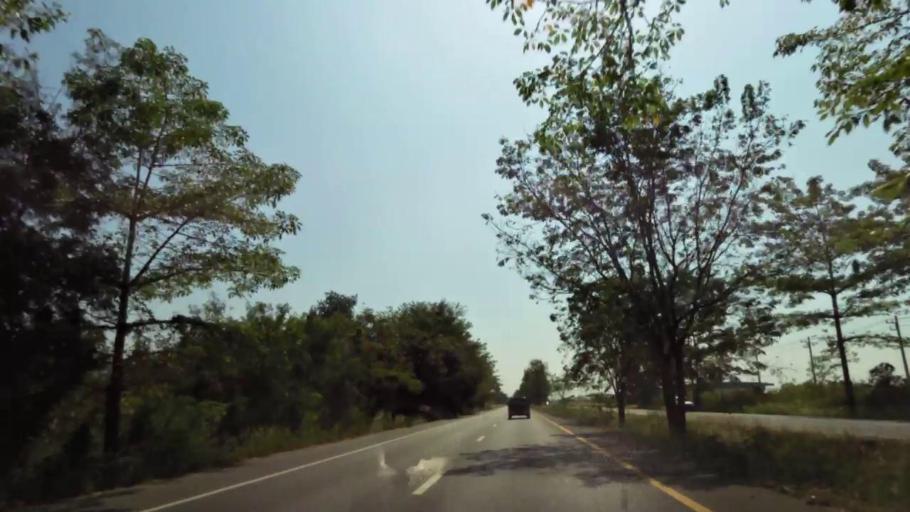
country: TH
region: Nakhon Sawan
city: Kao Liao
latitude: 15.9372
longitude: 100.1132
